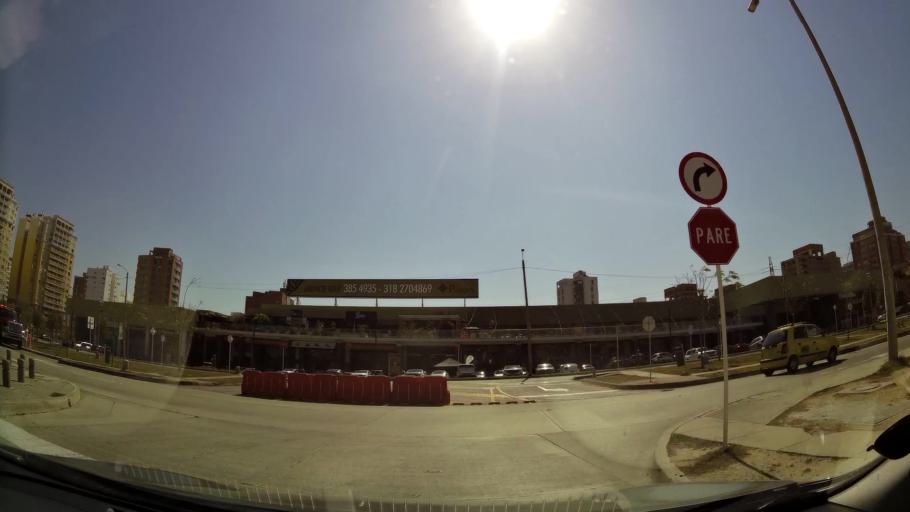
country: CO
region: Atlantico
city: Barranquilla
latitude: 11.0154
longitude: -74.8271
